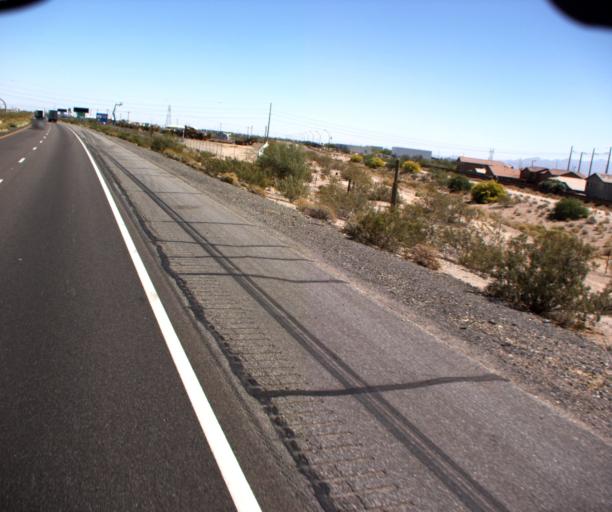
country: US
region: Arizona
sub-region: Maricopa County
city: Buckeye
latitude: 33.4283
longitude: -112.6068
